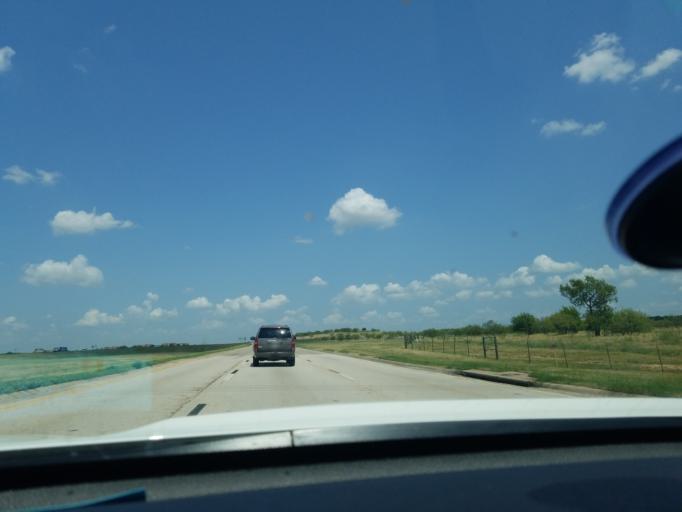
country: US
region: Texas
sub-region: Tarrant County
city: Keller
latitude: 32.9669
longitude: -97.2916
